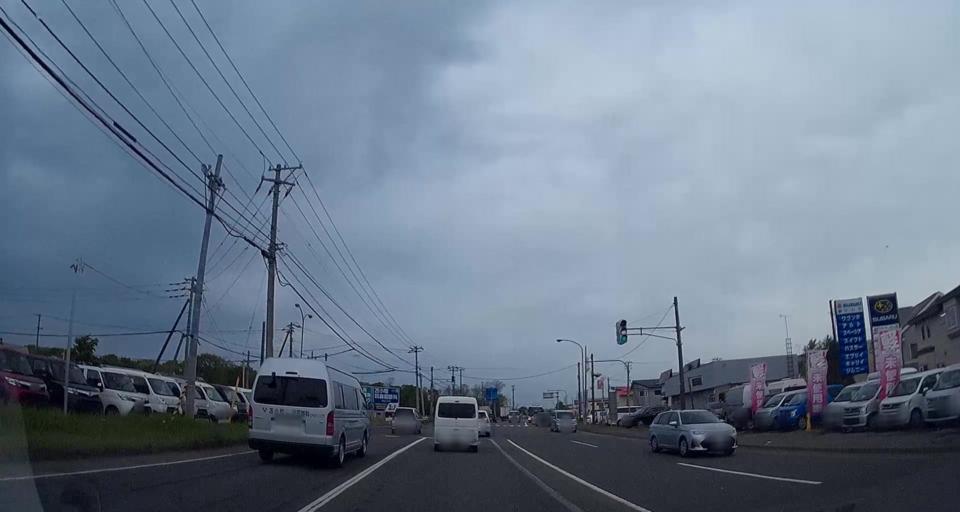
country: JP
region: Hokkaido
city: Tomakomai
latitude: 42.6717
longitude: 141.7036
